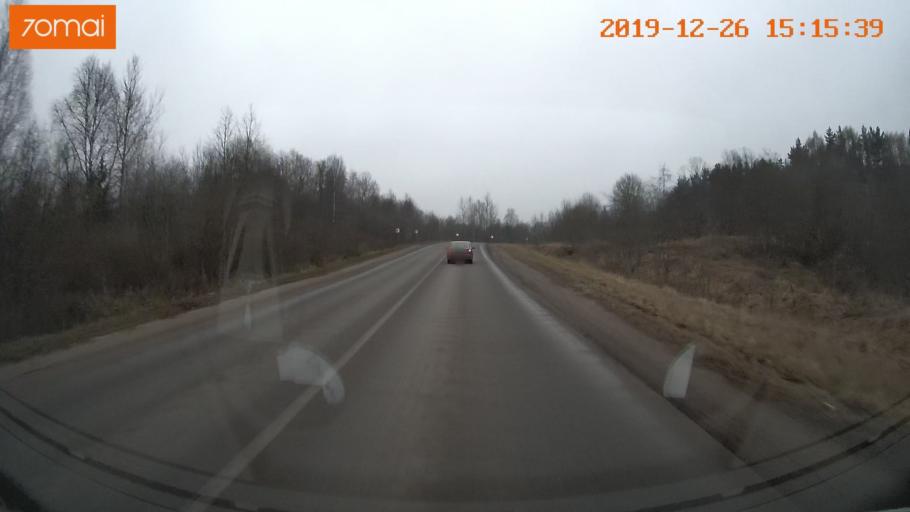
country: RU
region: Jaroslavl
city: Rybinsk
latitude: 58.0946
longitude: 38.8744
